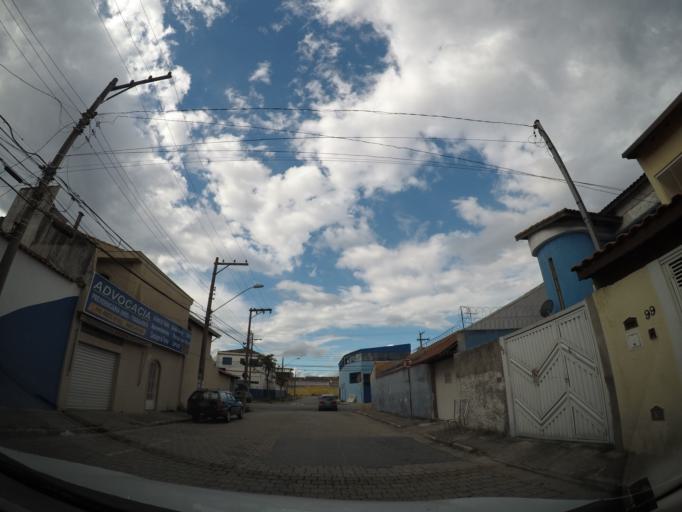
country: BR
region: Sao Paulo
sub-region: Guarulhos
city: Guarulhos
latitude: -23.4853
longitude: -46.5544
